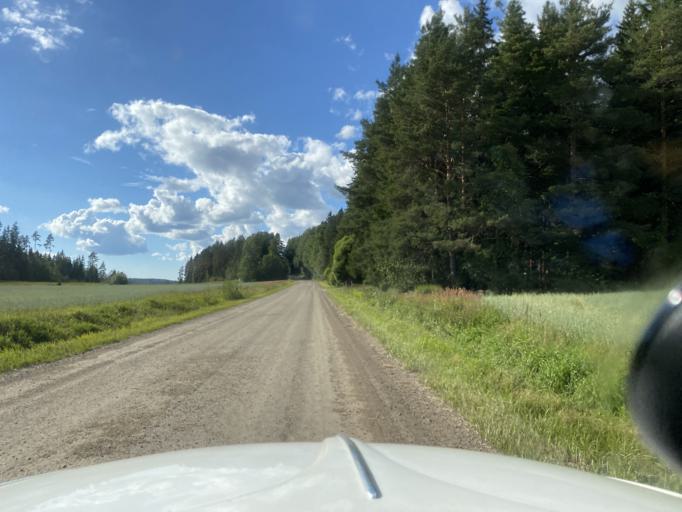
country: FI
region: Pirkanmaa
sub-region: Lounais-Pirkanmaa
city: Punkalaidun
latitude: 61.1378
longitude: 23.2182
